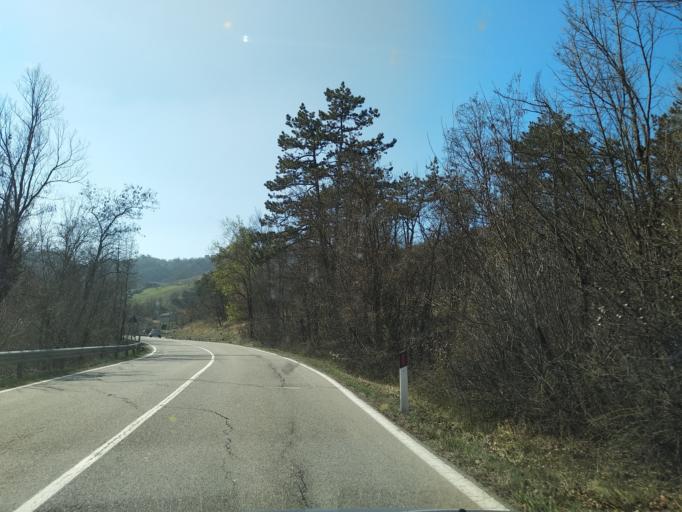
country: IT
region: Emilia-Romagna
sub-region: Provincia di Reggio Emilia
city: Vezzano sul Crostolo
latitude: 44.5797
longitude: 10.5307
